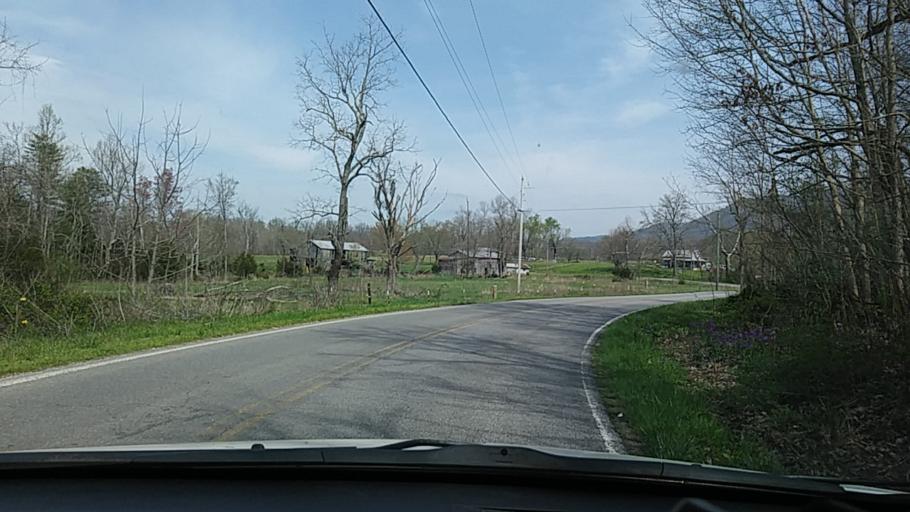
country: US
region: Tennessee
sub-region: Greene County
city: Tusculum
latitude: 36.0966
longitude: -82.7110
